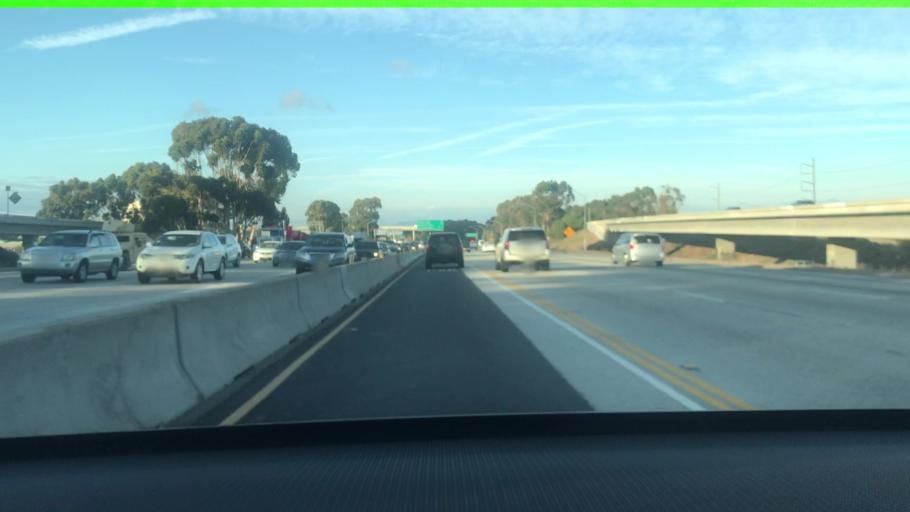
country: US
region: California
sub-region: Los Angeles County
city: Del Aire
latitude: 33.9180
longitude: -118.3699
